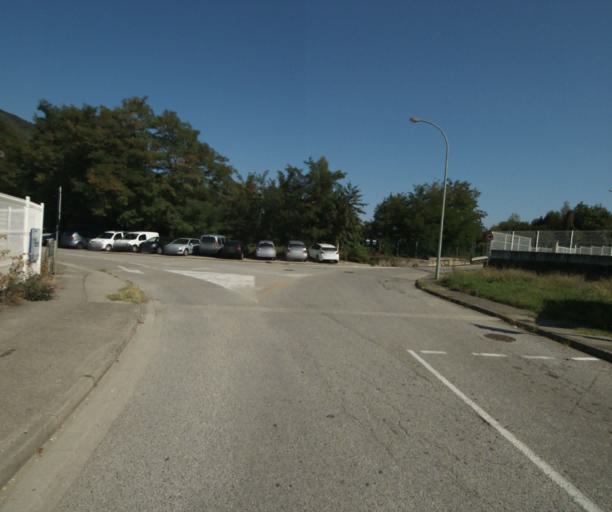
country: FR
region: Rhone-Alpes
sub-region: Departement de l'Isere
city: Le Pont-de-Claix
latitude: 45.1386
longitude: 5.6959
